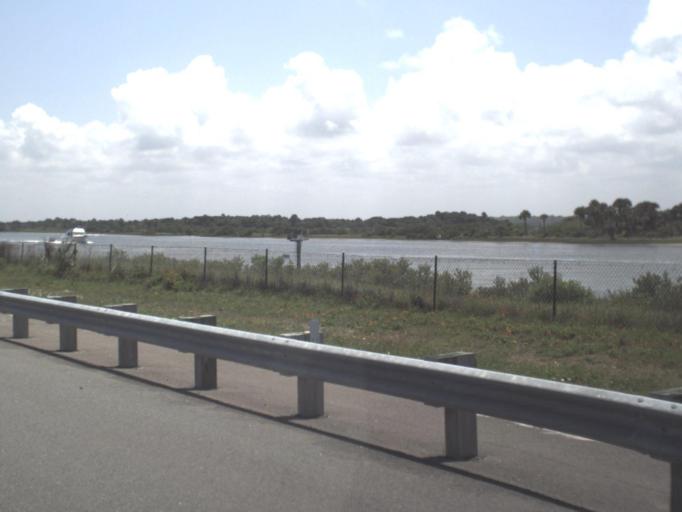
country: US
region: Florida
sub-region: Flagler County
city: Palm Coast
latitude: 29.6892
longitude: -81.2233
